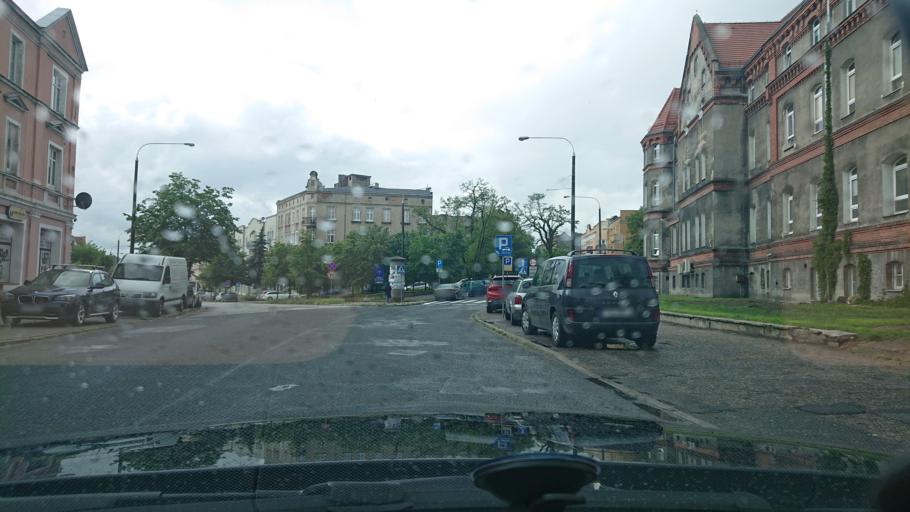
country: PL
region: Greater Poland Voivodeship
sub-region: Powiat gnieznienski
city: Gniezno
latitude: 52.5411
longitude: 17.6003
